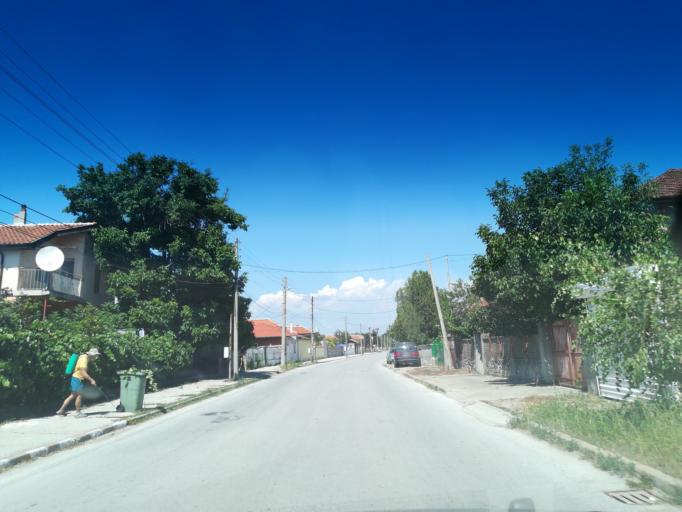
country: BG
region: Plovdiv
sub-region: Obshtina Sadovo
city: Sadovo
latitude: 42.0296
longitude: 25.1139
